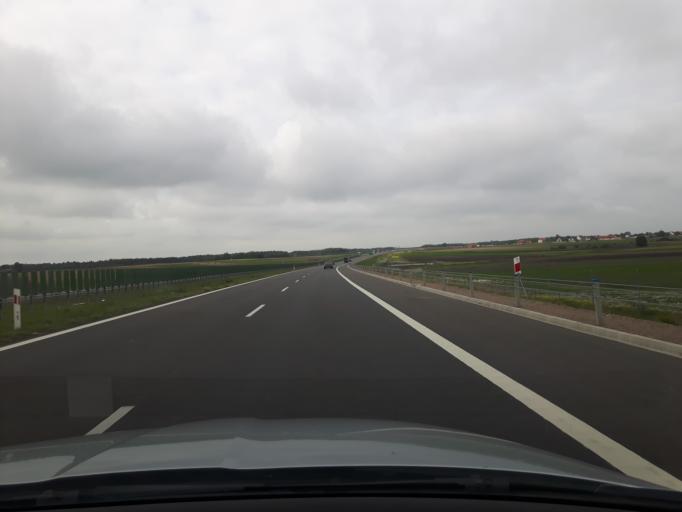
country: PL
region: Swietokrzyskie
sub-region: Powiat jedrzejowski
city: Sobkow
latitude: 50.6955
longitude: 20.3887
